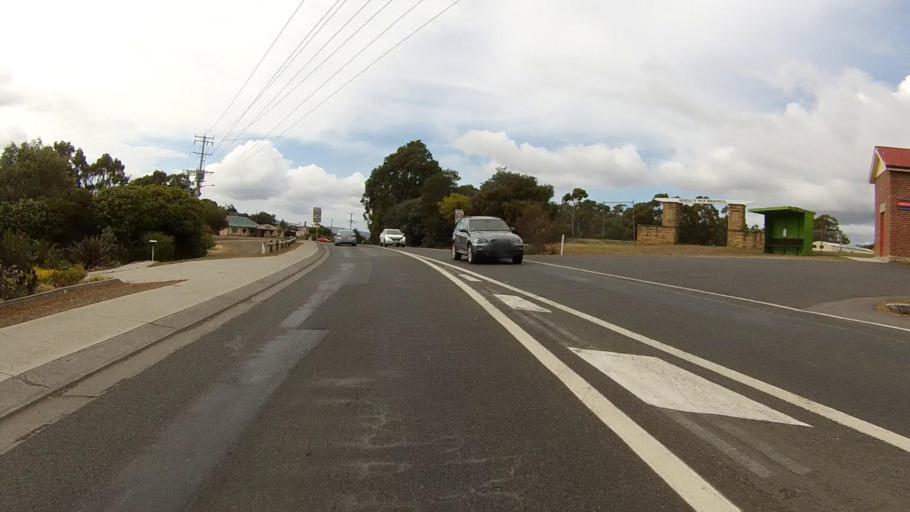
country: AU
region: Tasmania
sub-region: Kingborough
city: Margate
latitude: -43.0288
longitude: 147.2631
